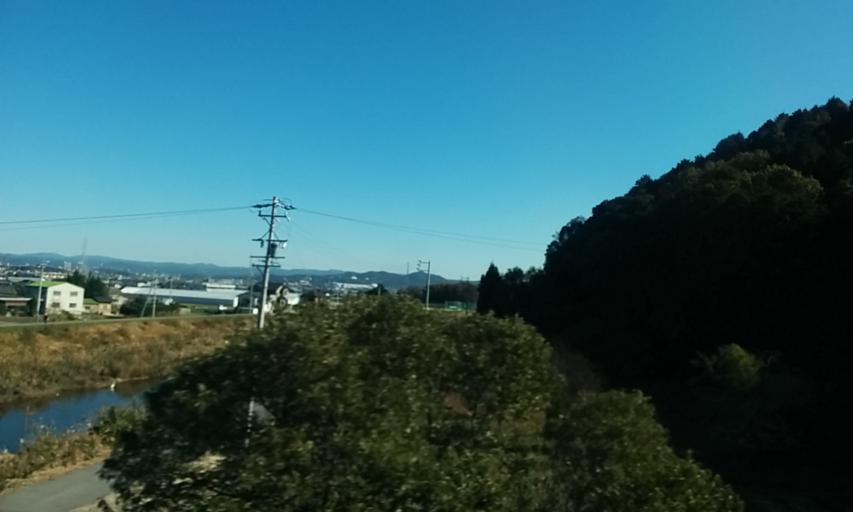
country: JP
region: Aichi
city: Okazaki
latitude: 34.8899
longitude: 137.1333
